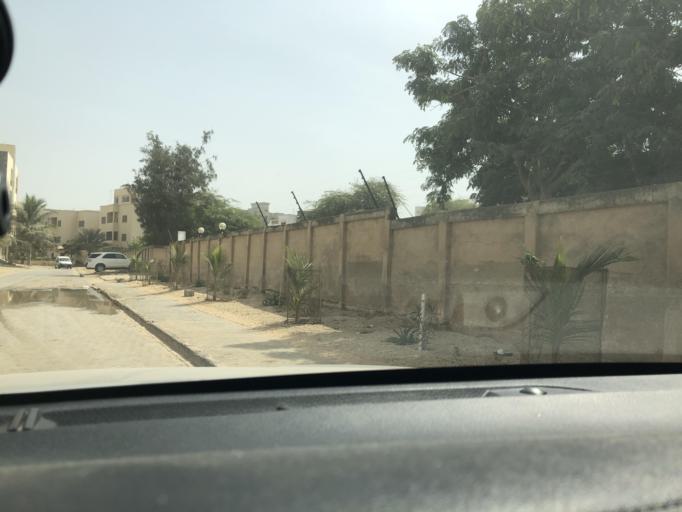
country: SN
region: Dakar
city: Mermoz Boabab
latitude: 14.7450
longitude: -17.5165
